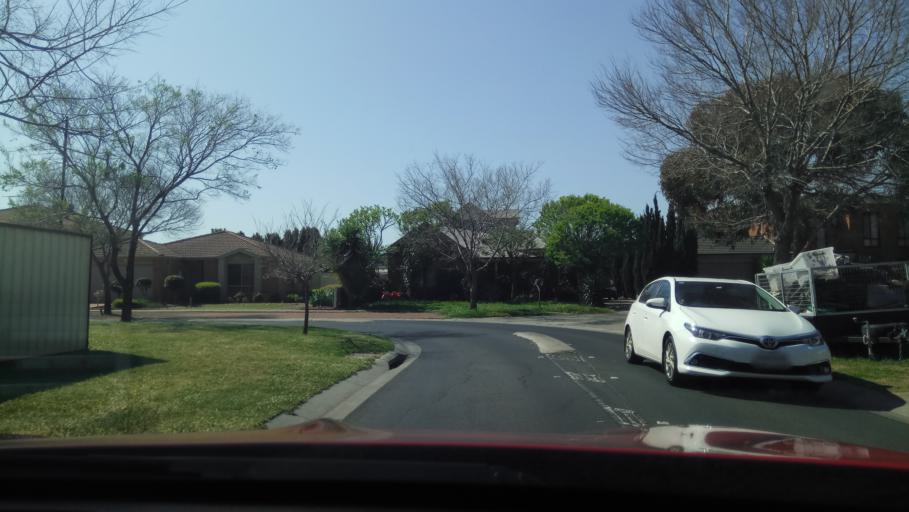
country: AU
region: Victoria
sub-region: Wyndham
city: Williams Landing
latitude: -37.8832
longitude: 144.7519
